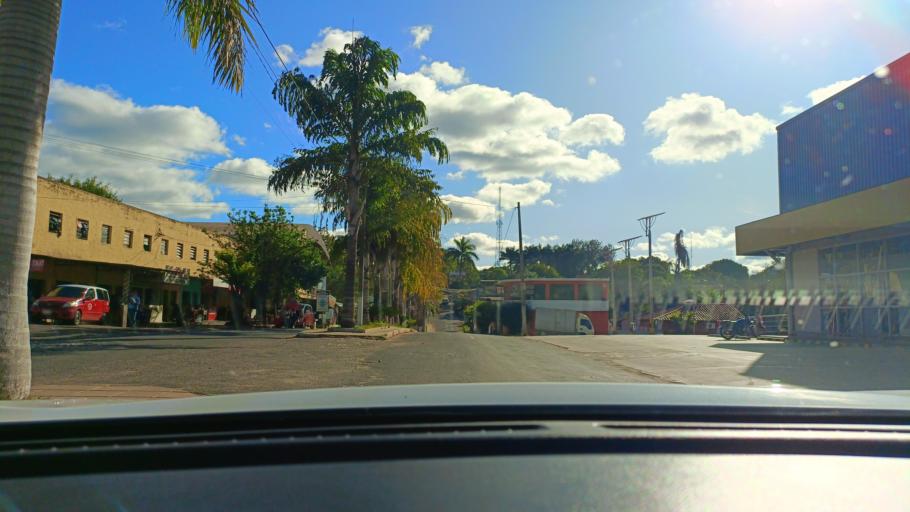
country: PY
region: San Pedro
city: Guayaybi
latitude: -24.6654
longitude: -56.4395
